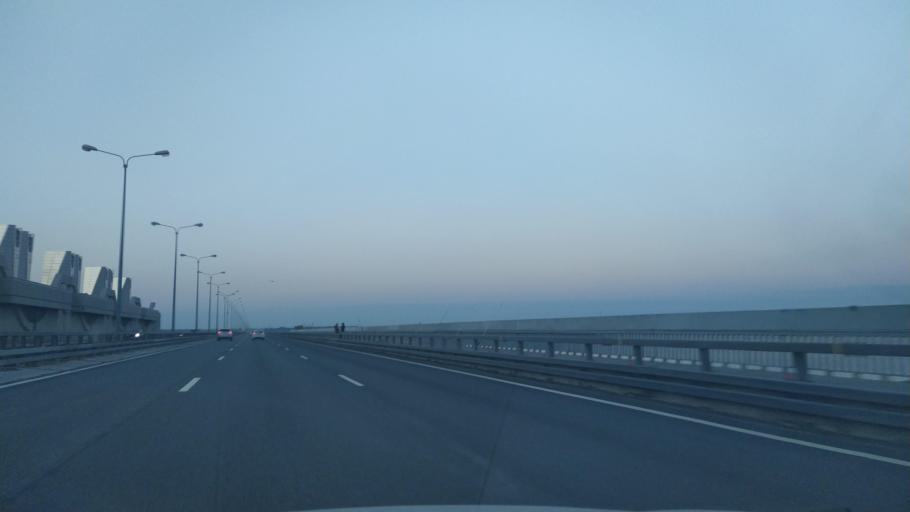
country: RU
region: Leningrad
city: Gorskaya
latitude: 60.0328
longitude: 29.9049
